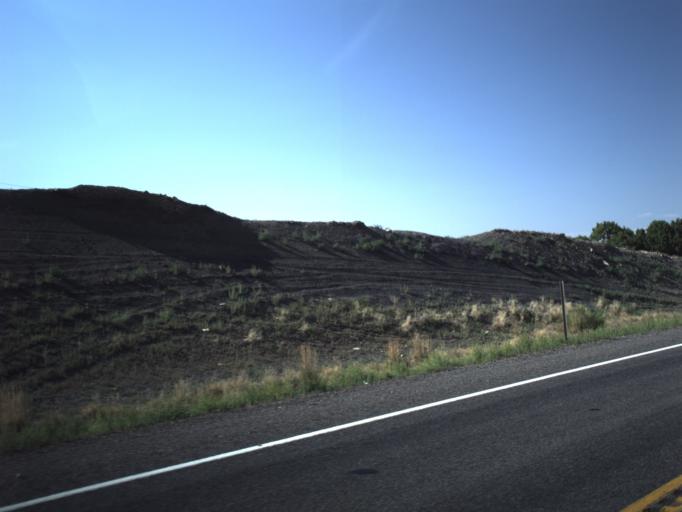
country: US
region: Utah
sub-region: Emery County
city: Castle Dale
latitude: 39.2129
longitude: -111.0008
